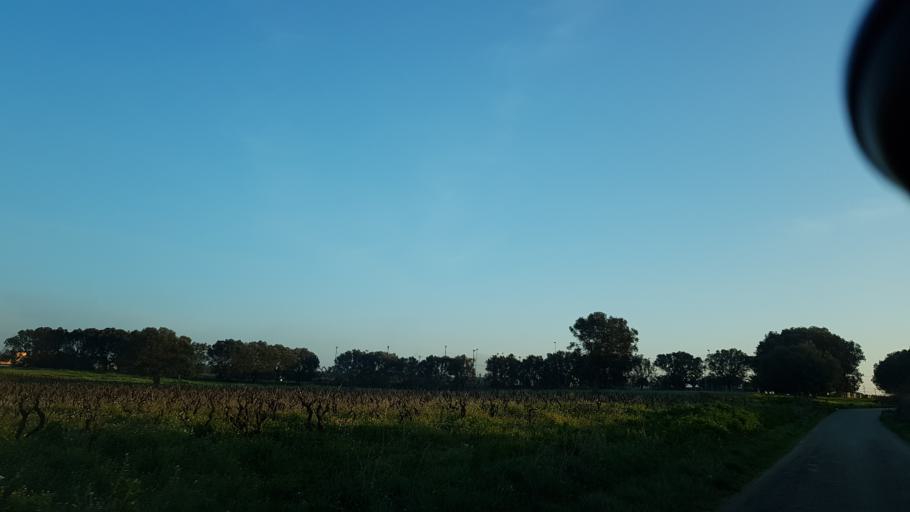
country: IT
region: Apulia
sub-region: Provincia di Brindisi
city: La Rosa
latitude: 40.6127
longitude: 17.9398
